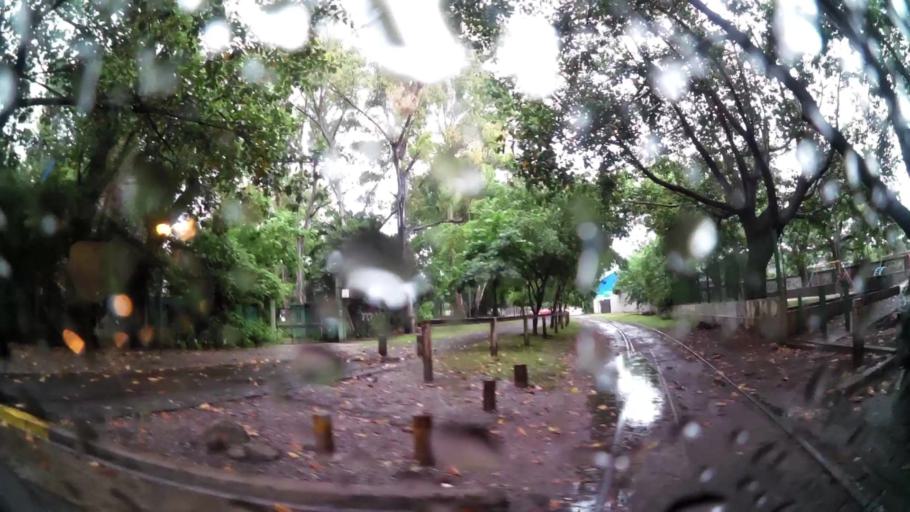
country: AR
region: Buenos Aires F.D.
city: Buenos Aires
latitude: -34.6264
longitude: -58.3634
